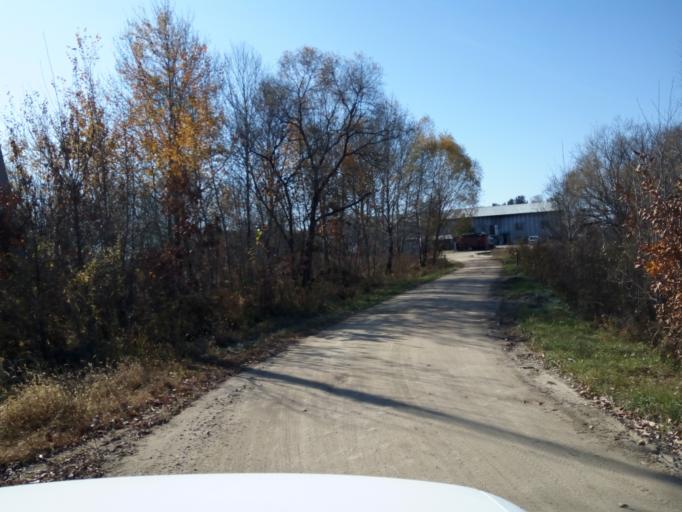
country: RU
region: Primorskiy
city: Dal'nerechensk
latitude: 45.9120
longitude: 133.8081
